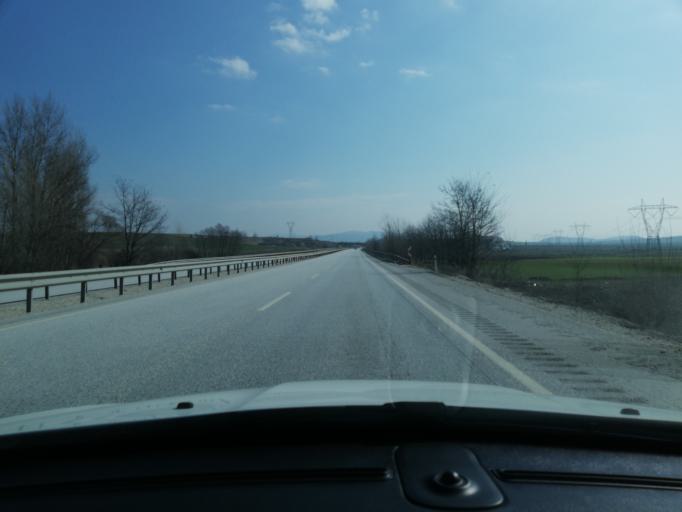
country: TR
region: Cankiri
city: Atkaracalar
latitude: 40.8388
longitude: 33.1590
